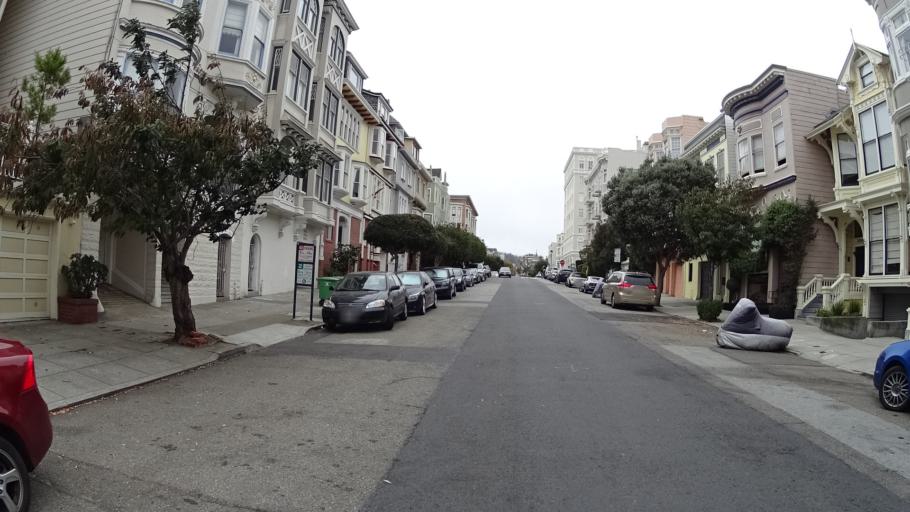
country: US
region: California
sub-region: San Francisco County
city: San Francisco
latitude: 37.7965
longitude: -122.4326
